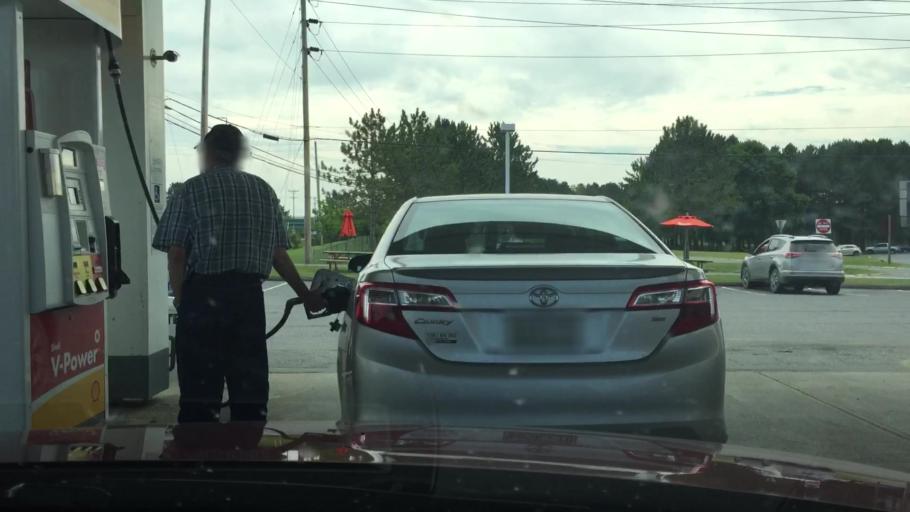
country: US
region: Maine
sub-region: Aroostook County
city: Houlton
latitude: 46.1420
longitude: -67.8408
